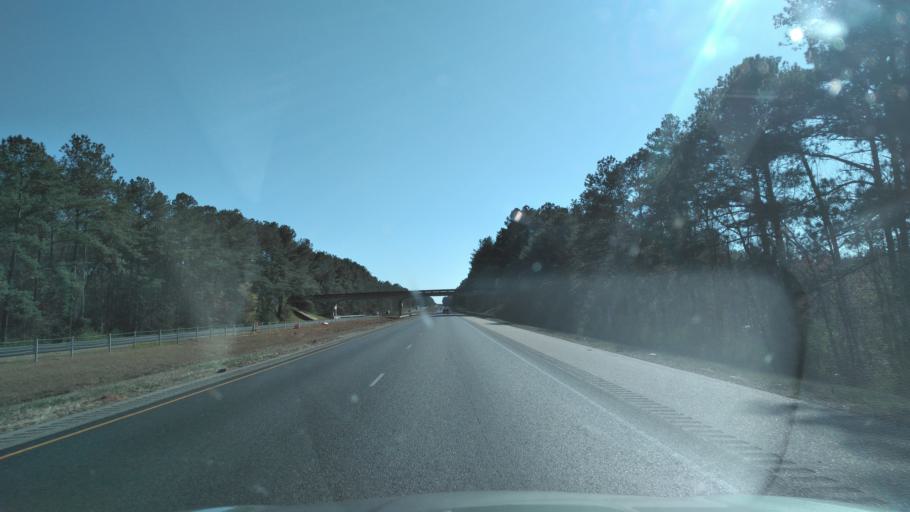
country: US
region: Alabama
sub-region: Butler County
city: Georgiana
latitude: 31.7293
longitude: -86.7214
